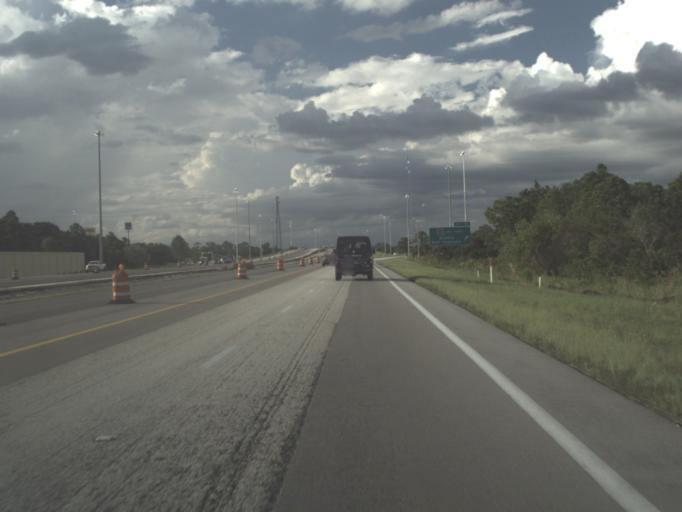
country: US
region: Florida
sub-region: Charlotte County
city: Harbour Heights
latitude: 27.0144
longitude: -82.0446
